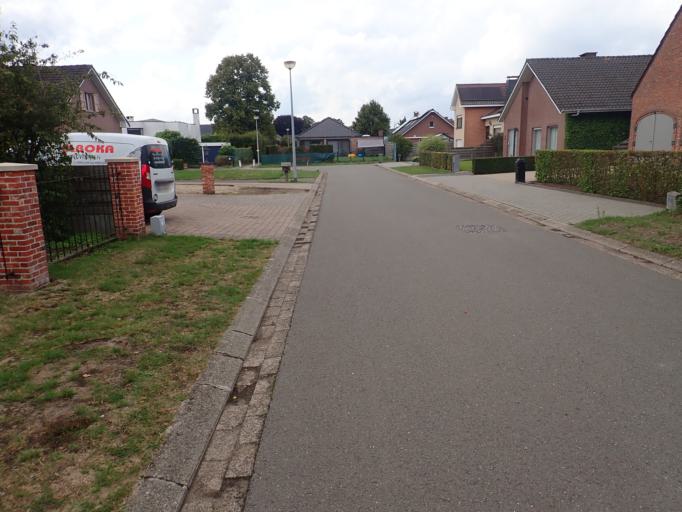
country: BE
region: Flanders
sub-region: Provincie Antwerpen
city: Lille
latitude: 51.2592
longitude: 4.7909
